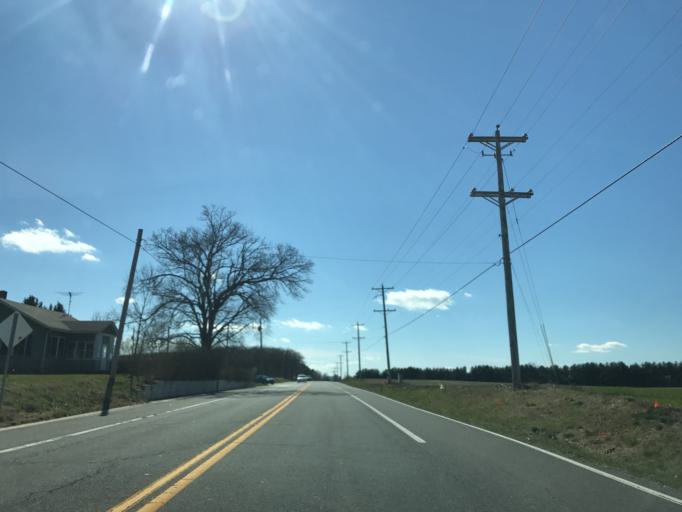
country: US
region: Maryland
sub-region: Kent County
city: Chestertown
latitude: 39.2158
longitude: -76.0911
